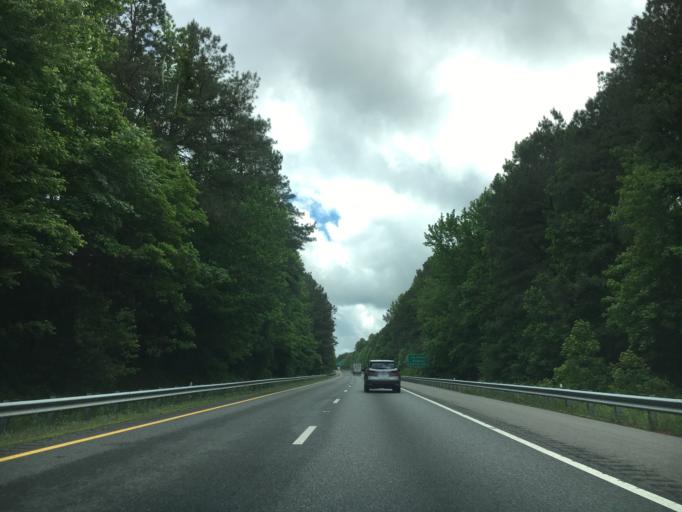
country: US
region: Virginia
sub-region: Mecklenburg County
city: South Hill
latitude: 36.7237
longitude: -78.1089
